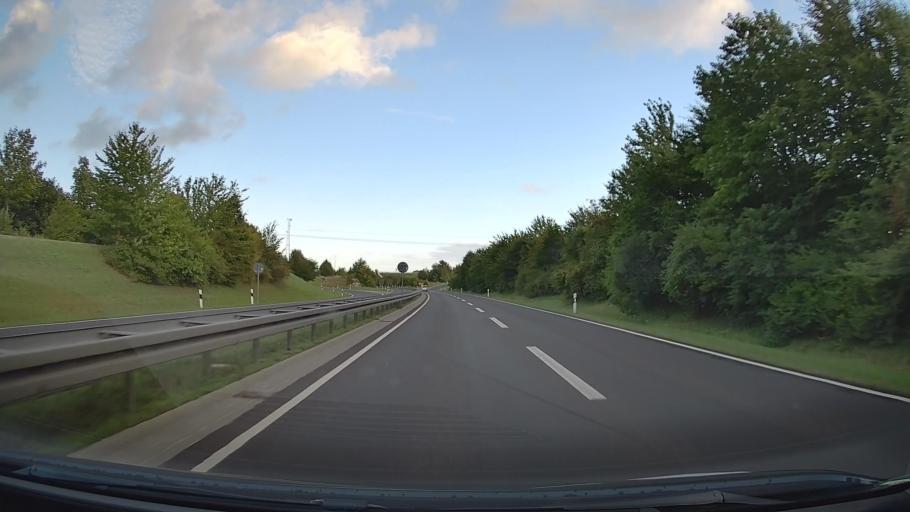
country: DE
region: Mecklenburg-Vorpommern
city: Stralsund
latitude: 54.2866
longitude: 13.0690
